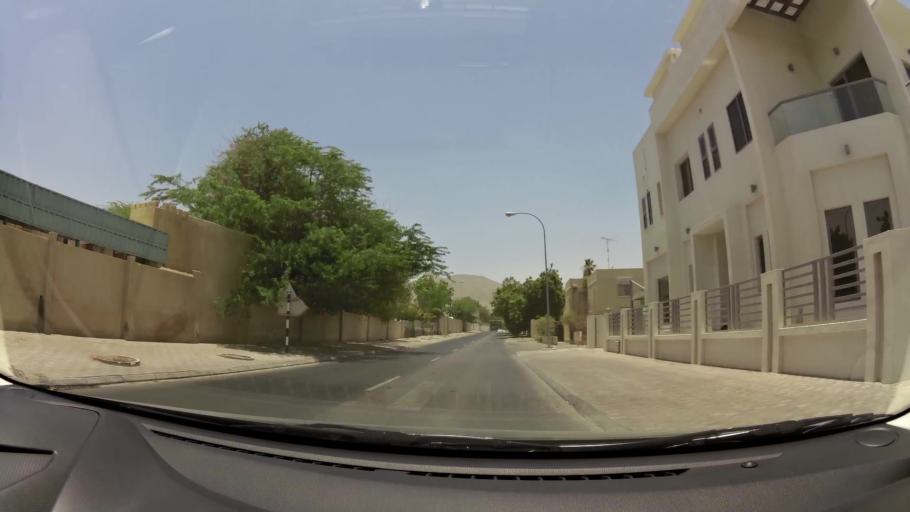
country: OM
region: Muhafazat Masqat
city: Bawshar
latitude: 23.5995
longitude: 58.4495
